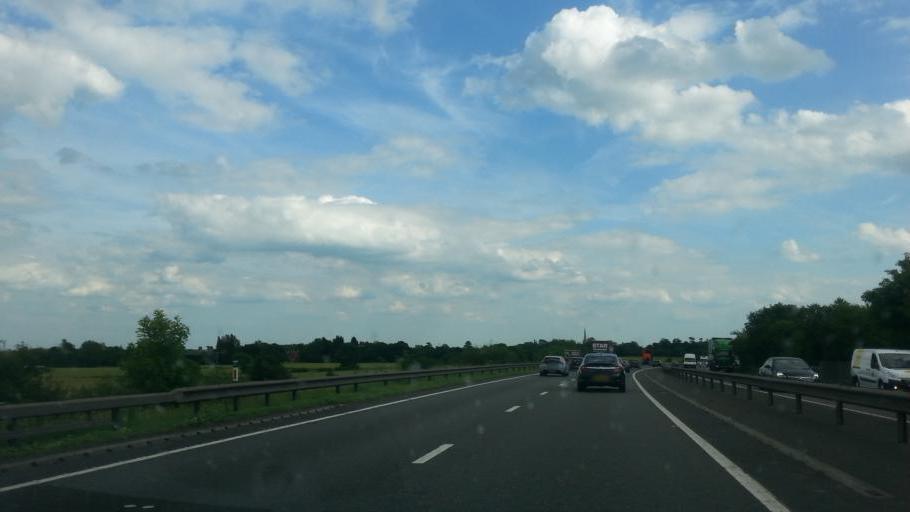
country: GB
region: England
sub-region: Nottinghamshire
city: South Collingham
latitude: 53.1754
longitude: -0.8149
